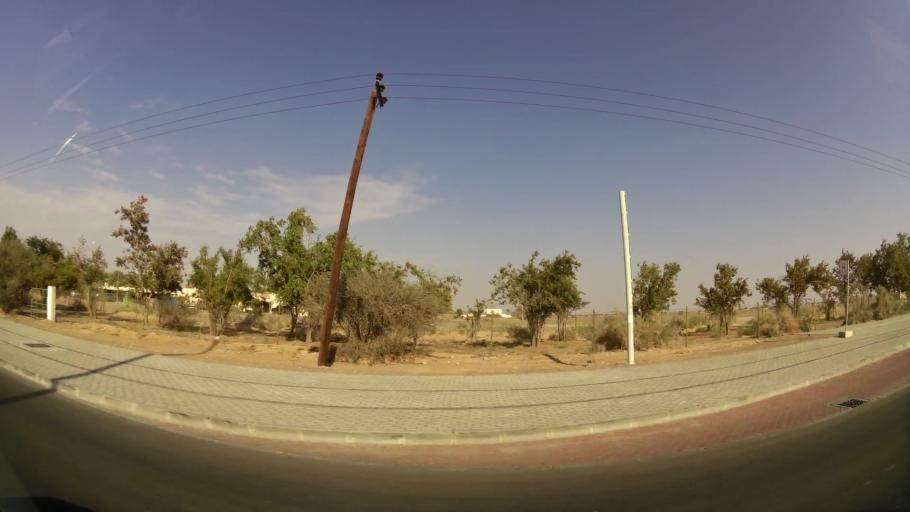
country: AE
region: Abu Dhabi
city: Al Ain
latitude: 24.0310
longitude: 55.8455
